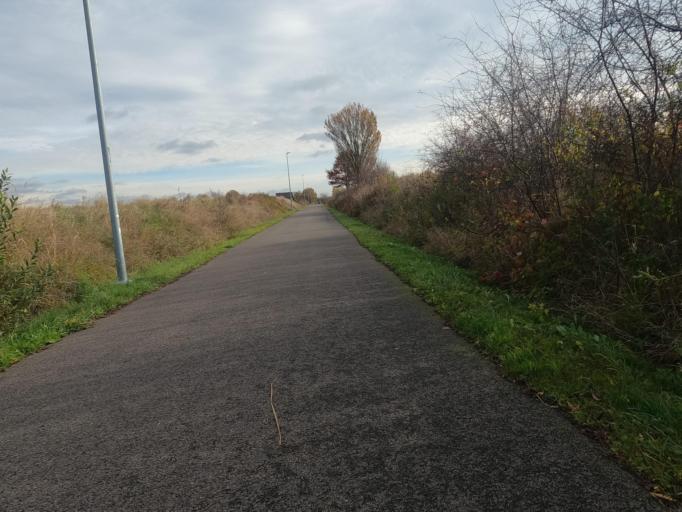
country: PL
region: Pomeranian Voivodeship
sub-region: Powiat starogardzki
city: Starogard Gdanski
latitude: 53.9801
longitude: 18.4802
